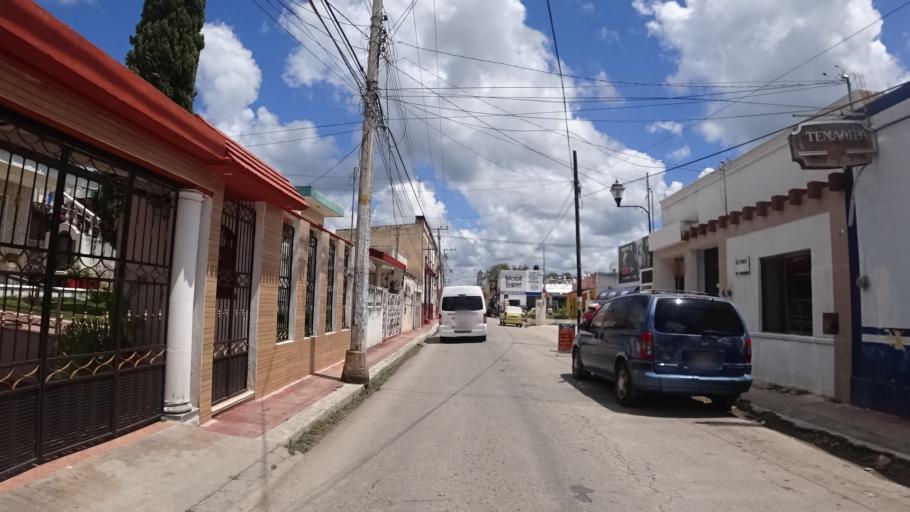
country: MX
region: Yucatan
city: Valladolid
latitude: 20.6898
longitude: -88.2068
